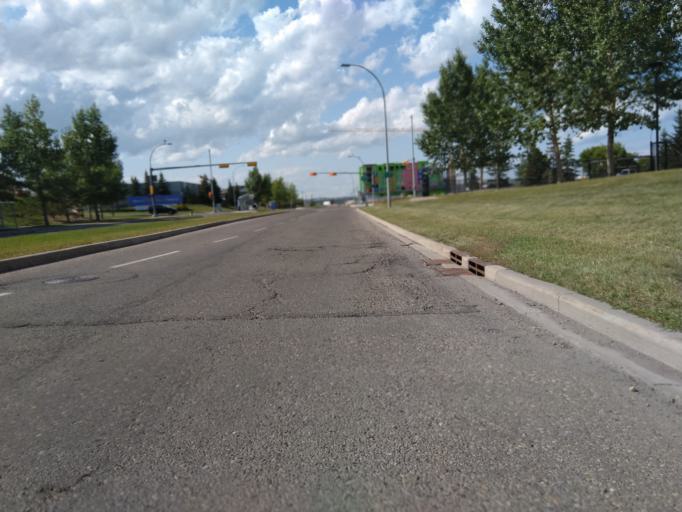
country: CA
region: Alberta
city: Calgary
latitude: 51.0745
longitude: -114.1448
